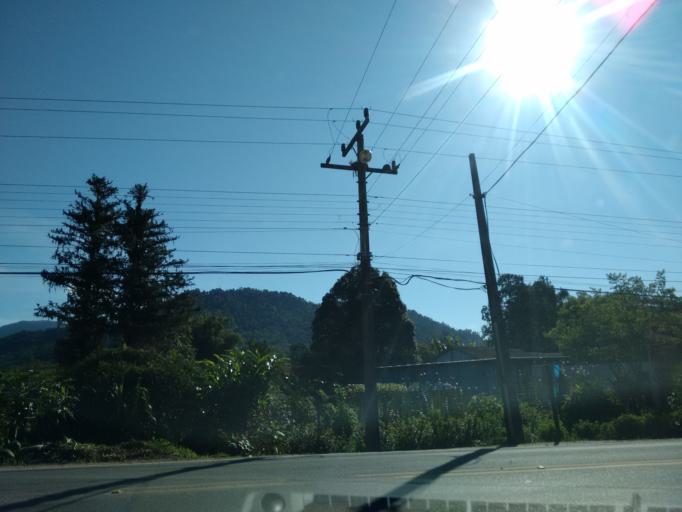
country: BR
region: Santa Catarina
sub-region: Pomerode
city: Pomerode
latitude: -26.6818
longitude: -49.1469
